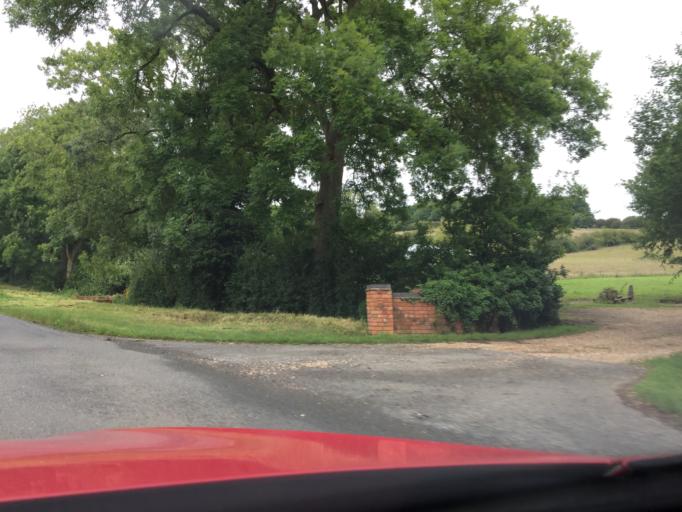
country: GB
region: England
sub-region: Northamptonshire
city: Daventry
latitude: 52.2426
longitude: -1.1942
